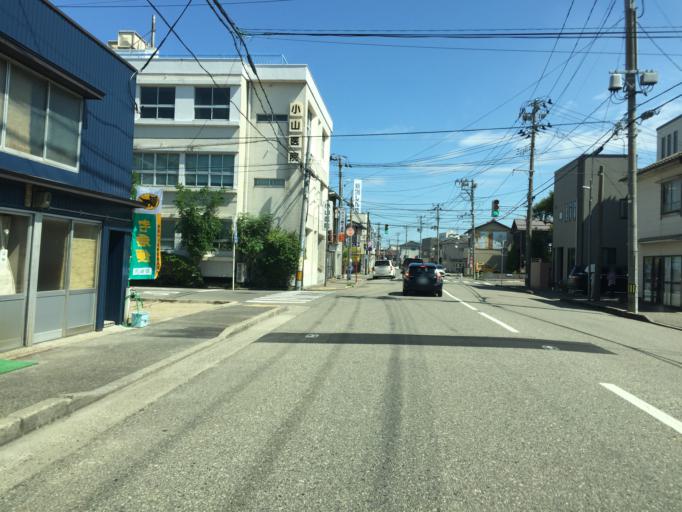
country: JP
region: Niigata
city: Niigata-shi
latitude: 37.9321
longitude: 139.0500
